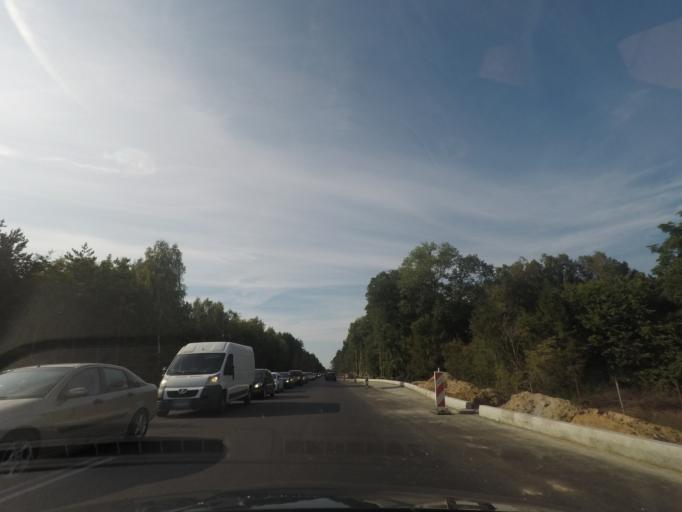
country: PL
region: Pomeranian Voivodeship
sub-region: Powiat leborski
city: Leba
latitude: 54.7138
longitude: 17.5778
